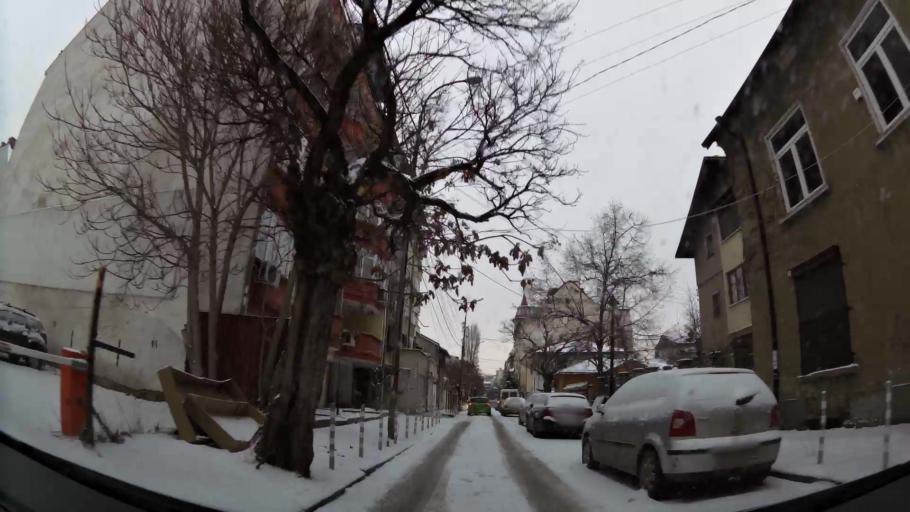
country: BG
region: Sofia-Capital
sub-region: Stolichna Obshtina
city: Sofia
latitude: 42.7028
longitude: 23.3070
